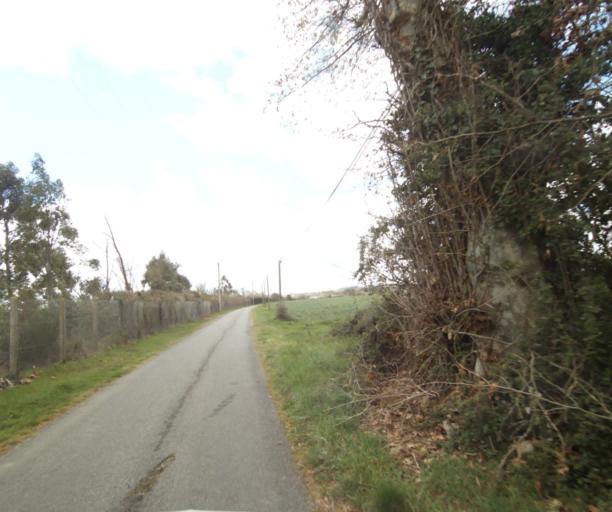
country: FR
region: Midi-Pyrenees
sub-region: Departement de l'Ariege
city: Saverdun
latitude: 43.2427
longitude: 1.5953
